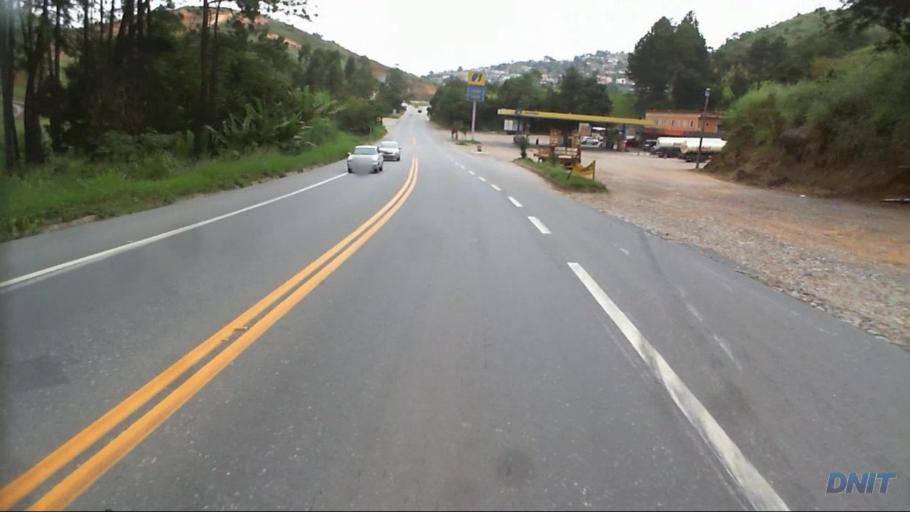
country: BR
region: Minas Gerais
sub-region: Nova Era
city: Nova Era
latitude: -19.7466
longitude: -43.0233
